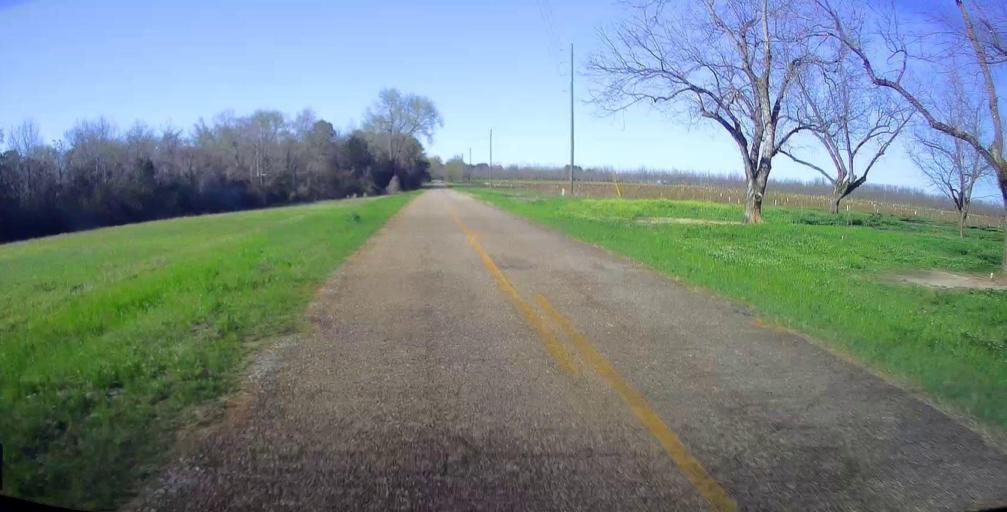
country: US
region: Georgia
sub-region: Macon County
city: Marshallville
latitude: 32.4866
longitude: -83.9521
